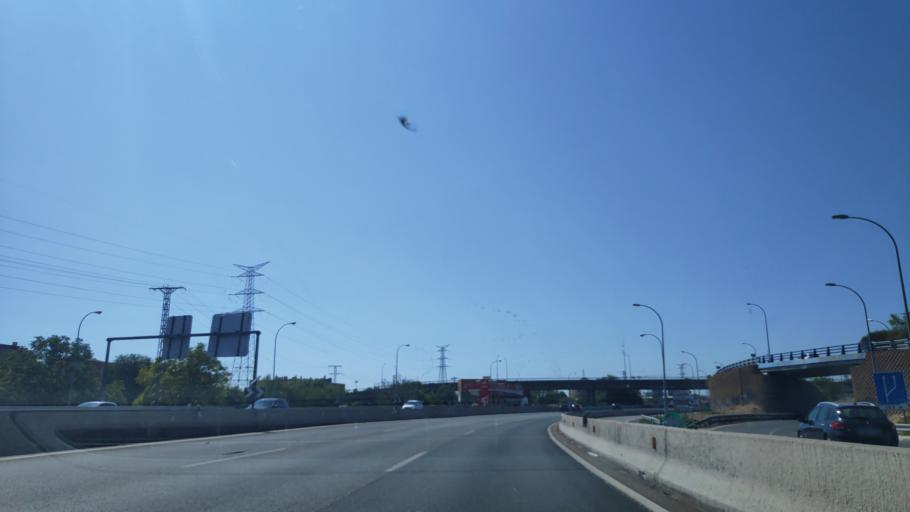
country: ES
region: Madrid
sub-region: Provincia de Madrid
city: Getafe
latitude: 40.3292
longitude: -3.7255
